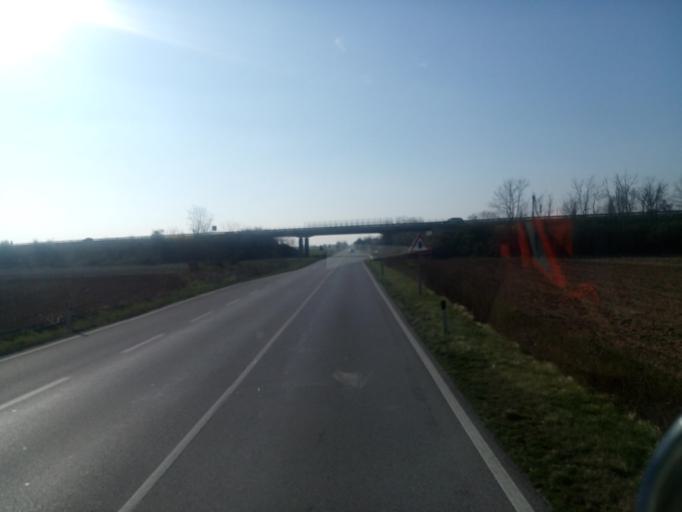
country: IT
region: Friuli Venezia Giulia
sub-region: Provincia di Udine
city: Bertiolo
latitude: 45.9450
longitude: 13.0868
